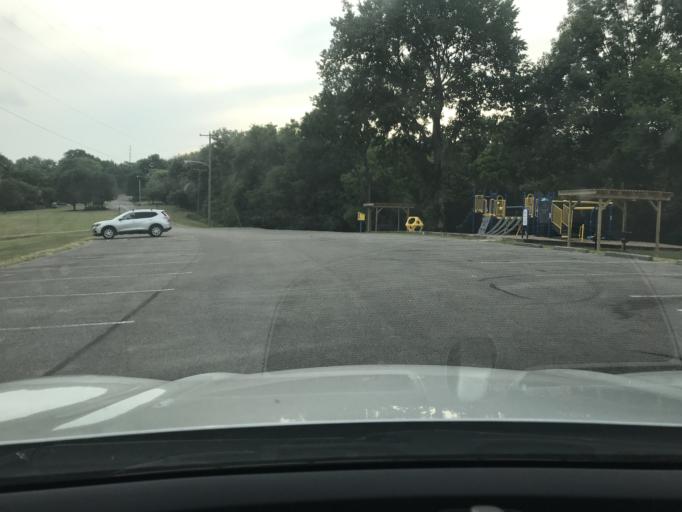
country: US
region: Tennessee
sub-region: Davidson County
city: Goodlettsville
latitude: 36.3058
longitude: -86.7089
